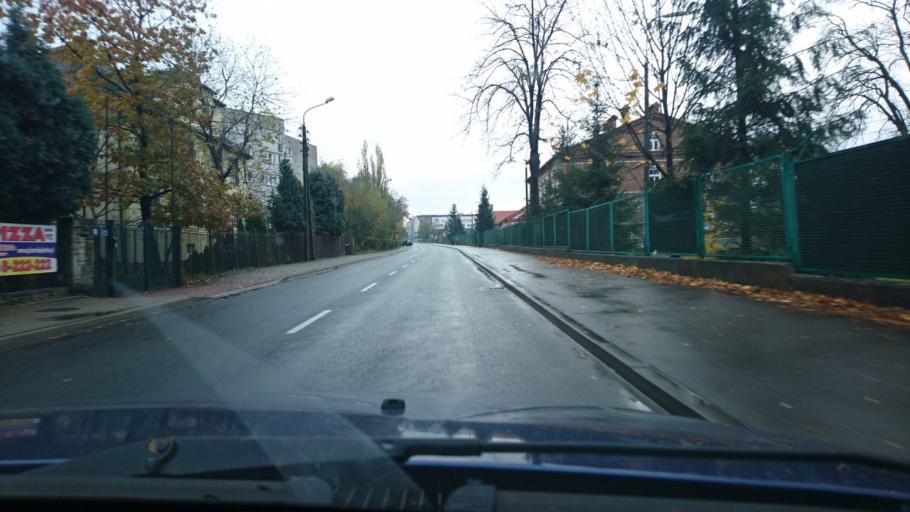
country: PL
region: Silesian Voivodeship
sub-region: Bielsko-Biala
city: Bielsko-Biala
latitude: 49.8068
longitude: 19.0483
